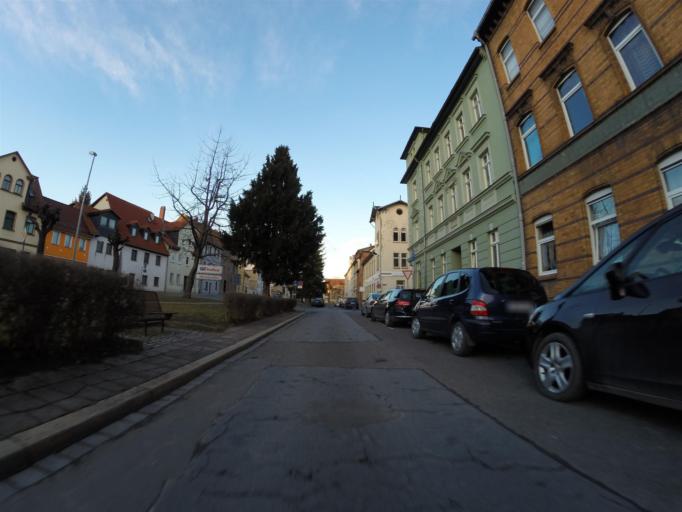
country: DE
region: Thuringia
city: Apolda
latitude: 51.0261
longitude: 11.5115
